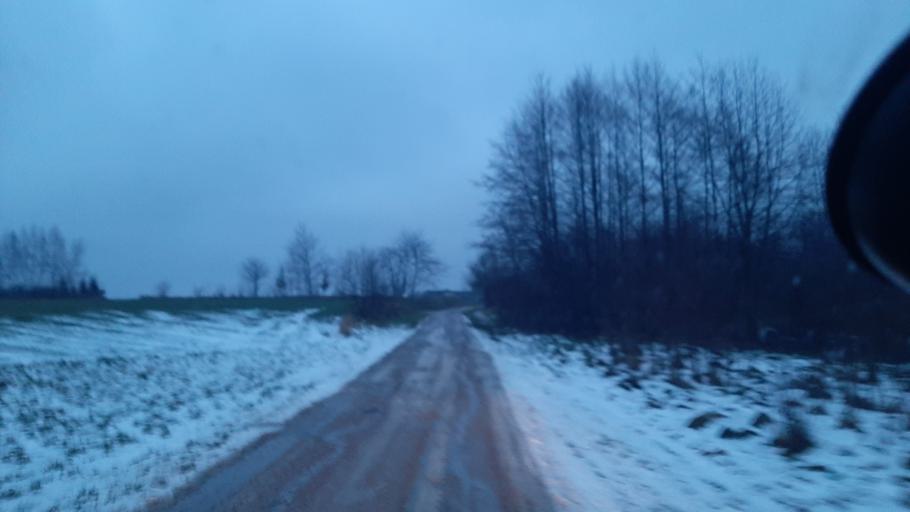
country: PL
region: Lublin Voivodeship
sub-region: Powiat lubelski
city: Jastkow
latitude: 51.3855
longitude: 22.4174
